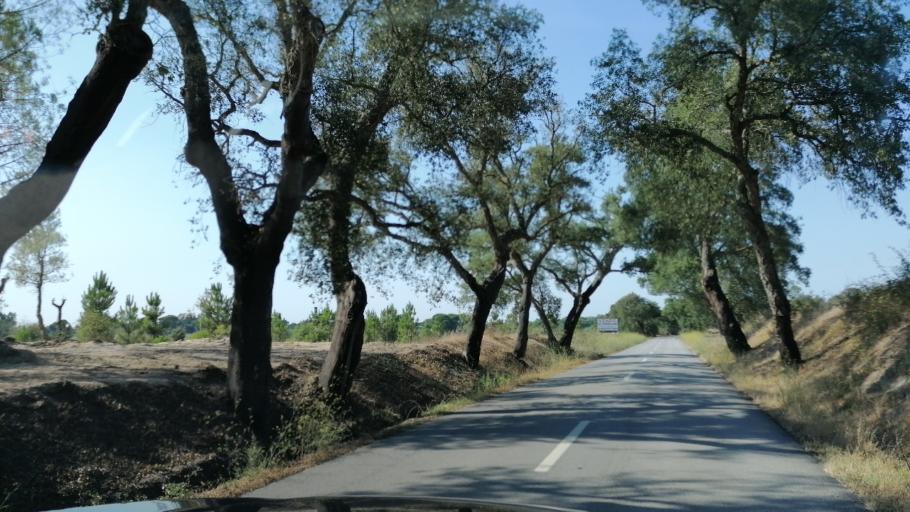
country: PT
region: Santarem
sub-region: Benavente
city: Poceirao
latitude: 38.7552
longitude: -8.6322
